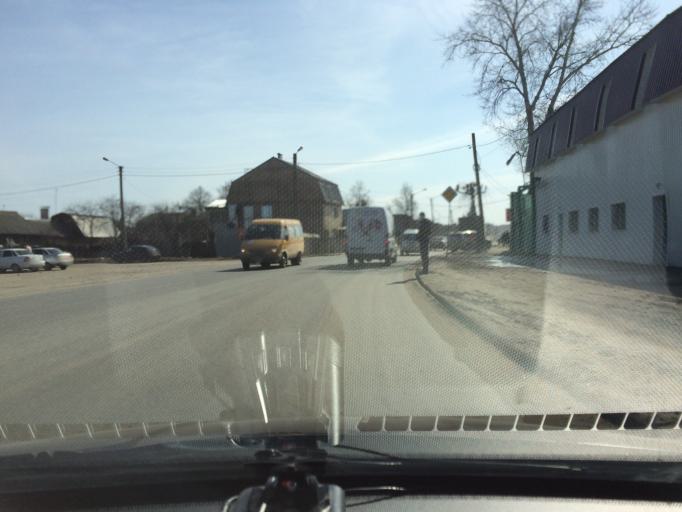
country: RU
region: Mariy-El
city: Yoshkar-Ola
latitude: 56.6488
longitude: 47.9019
